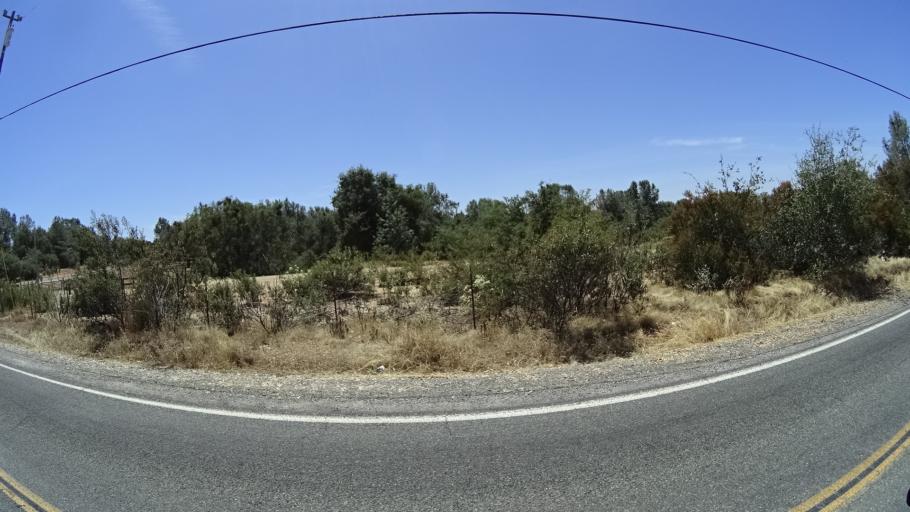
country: US
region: California
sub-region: Calaveras County
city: Valley Springs
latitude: 38.2124
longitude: -120.9087
